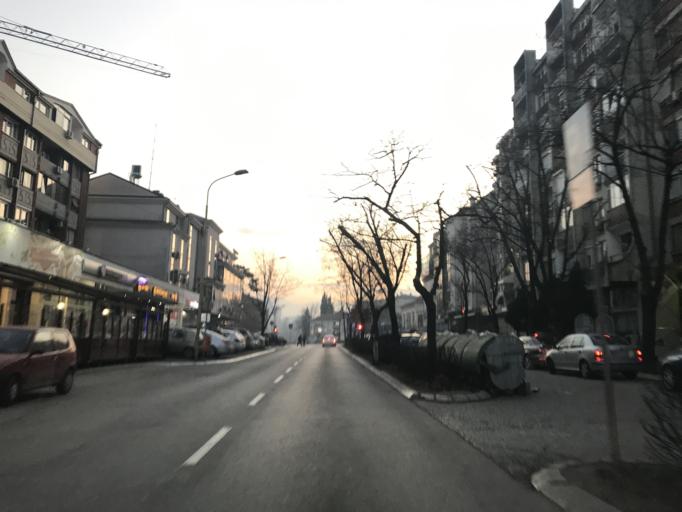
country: RS
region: Central Serbia
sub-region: Sumadijski Okrug
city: Kragujevac
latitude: 44.0134
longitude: 20.9127
